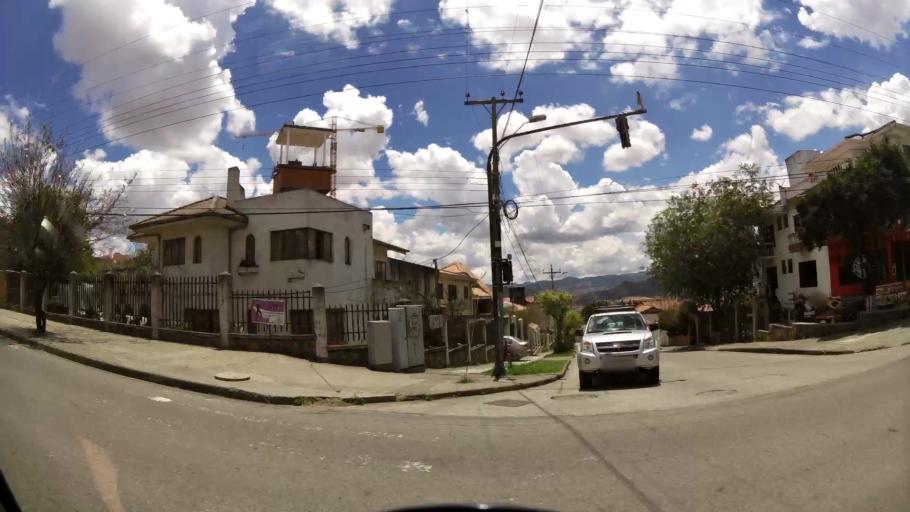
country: EC
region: Azuay
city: Cuenca
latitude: -2.8863
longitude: -79.0085
